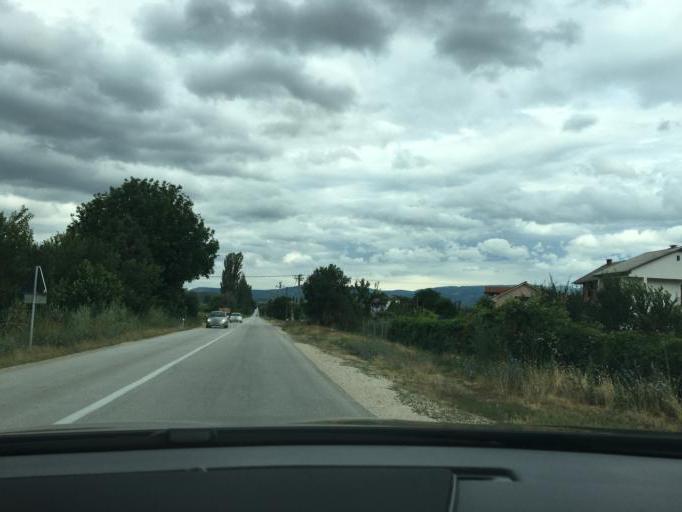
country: MK
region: Opstina Rankovce
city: Rankovce
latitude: 42.1700
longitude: 22.1581
